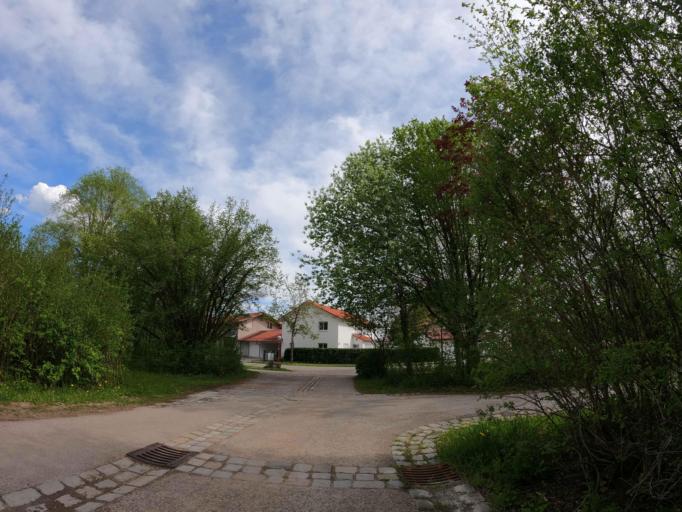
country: DE
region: Bavaria
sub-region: Upper Bavaria
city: Oberhaching
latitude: 48.0220
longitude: 11.5917
